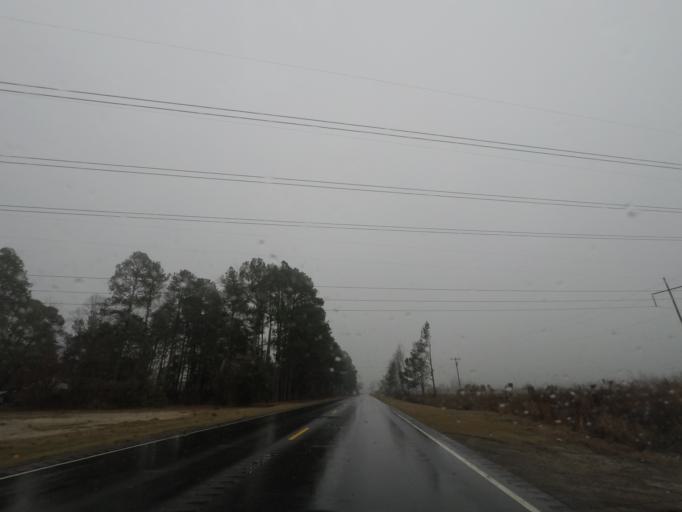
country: US
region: North Carolina
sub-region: Scotland County
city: Laurinburg
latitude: 34.8471
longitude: -79.4586
